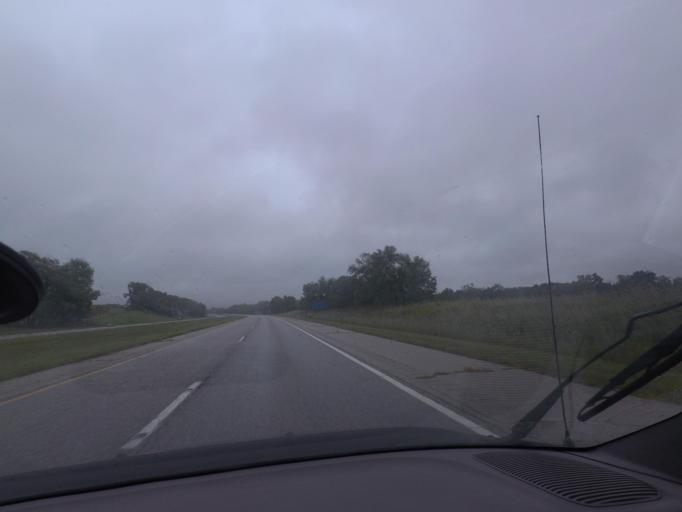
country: US
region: Illinois
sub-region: Pike County
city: Pittsfield
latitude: 39.6753
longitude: -90.8614
